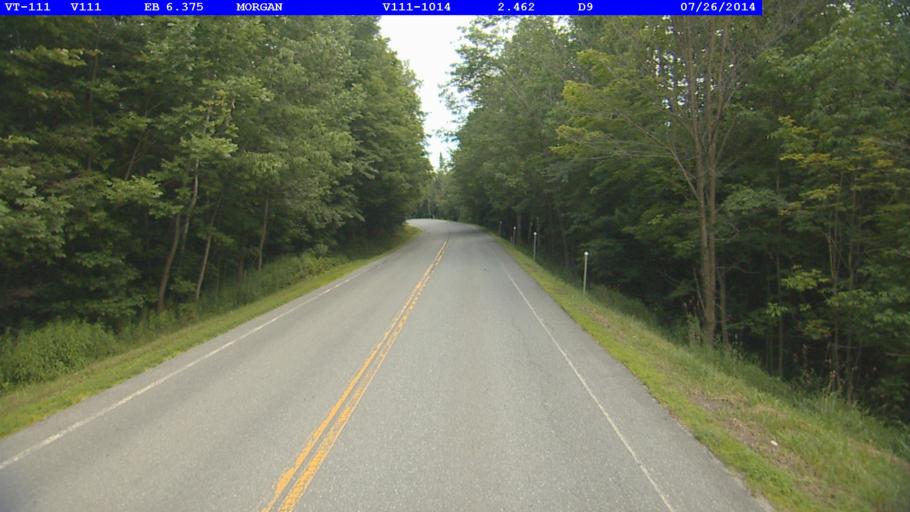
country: US
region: Vermont
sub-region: Orleans County
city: Newport
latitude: 44.9159
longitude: -72.0210
